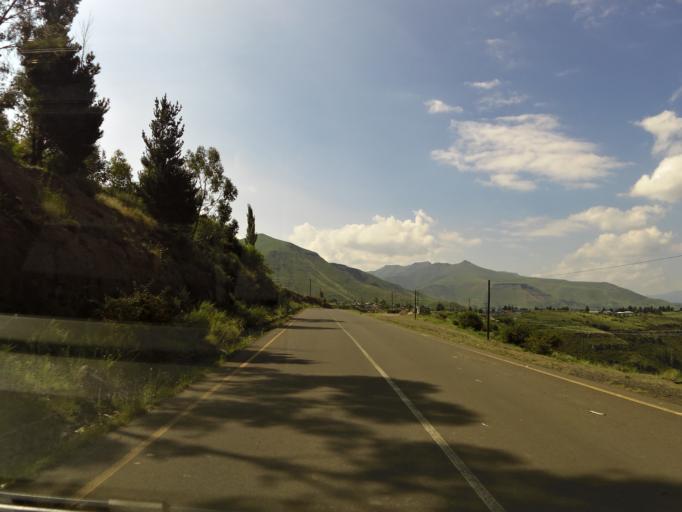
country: LS
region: Thaba-Tseka
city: Thaba-Tseka
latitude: -29.1167
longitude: 28.4912
